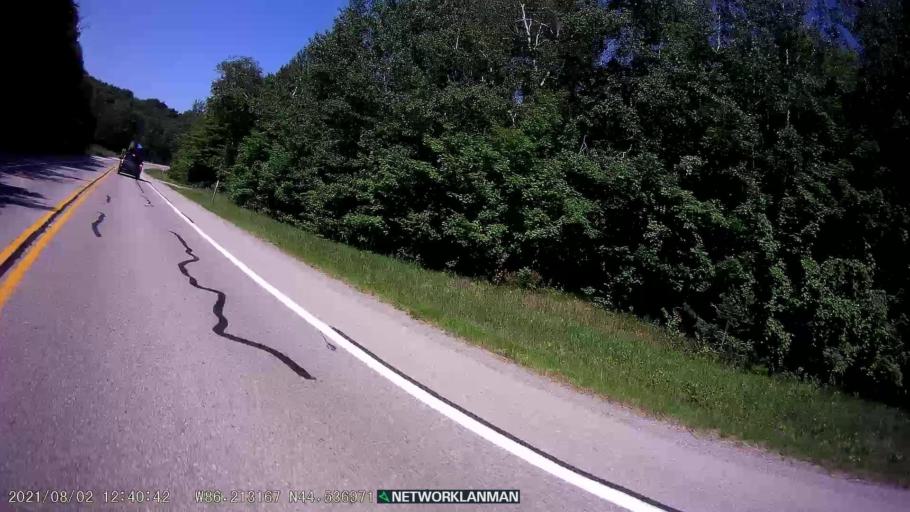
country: US
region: Michigan
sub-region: Benzie County
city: Frankfort
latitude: 44.5372
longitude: -86.2134
